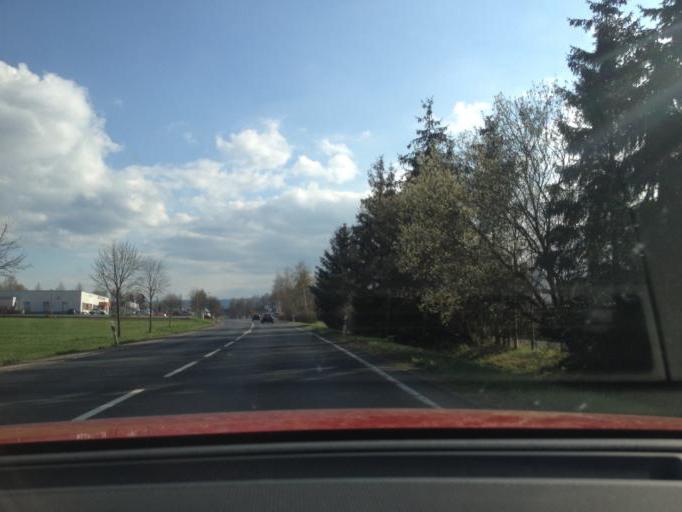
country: DE
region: Bavaria
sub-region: Upper Palatinate
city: Waldershof
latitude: 49.9914
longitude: 12.0685
